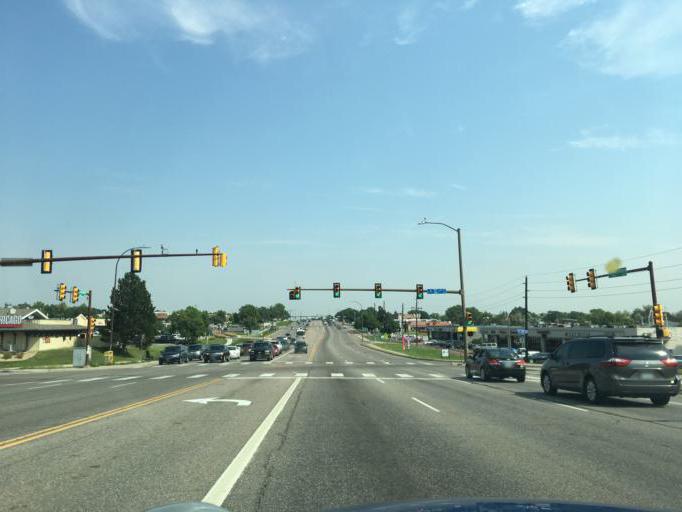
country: US
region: Colorado
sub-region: Adams County
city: Westminster
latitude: 39.8528
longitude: -105.0818
